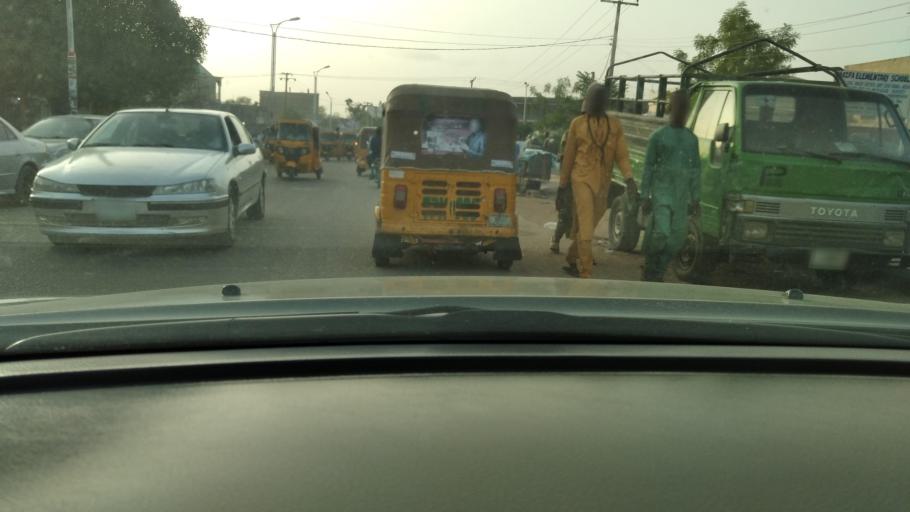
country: NG
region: Kano
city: Kano
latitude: 11.9629
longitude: 8.5263
